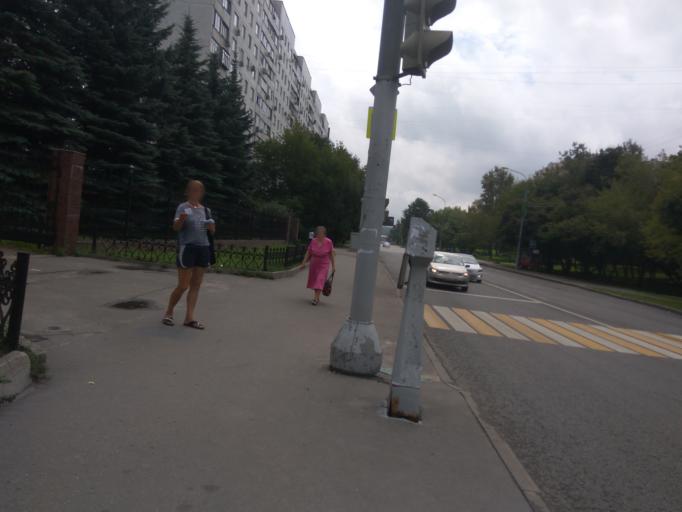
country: RU
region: Moscow
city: Tsaritsyno
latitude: 55.6262
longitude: 37.6656
